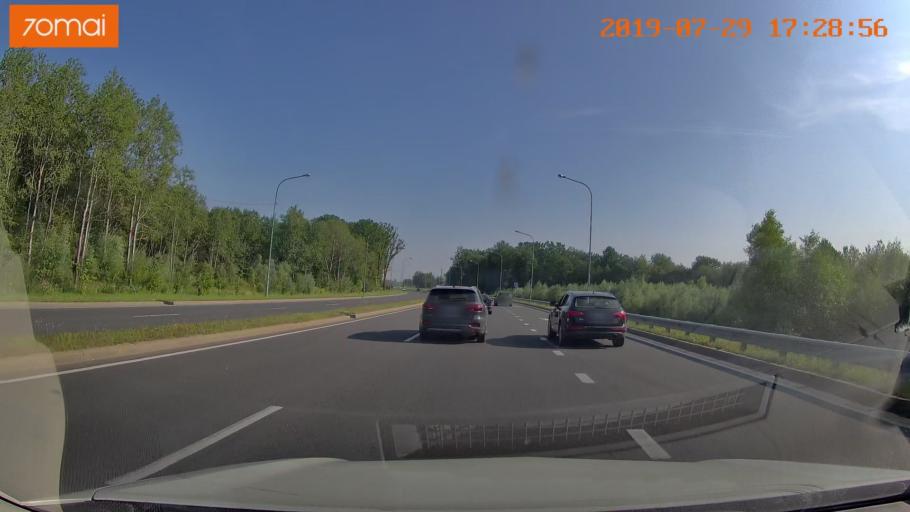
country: RU
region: Kaliningrad
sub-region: Gorod Kaliningrad
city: Kaliningrad
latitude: 54.7591
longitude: 20.4705
